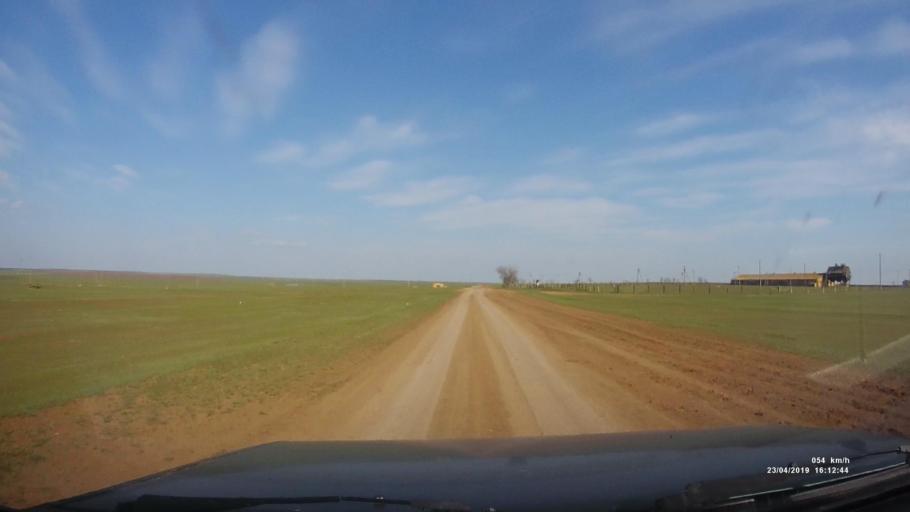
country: RU
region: Kalmykiya
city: Priyutnoye
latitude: 46.4653
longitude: 43.1294
